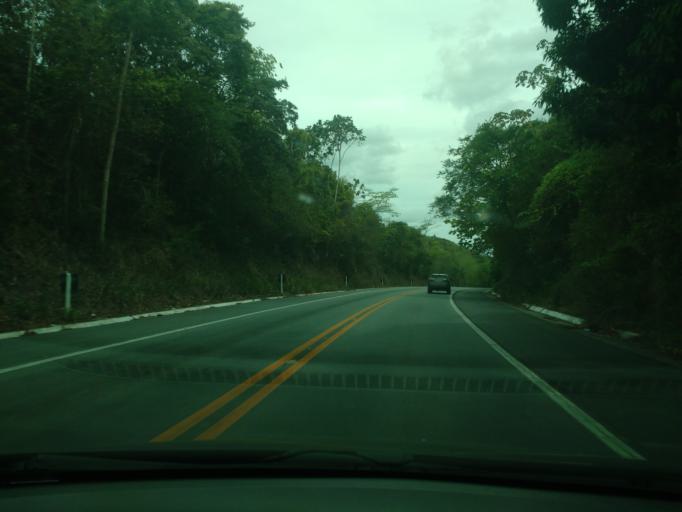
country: BR
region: Alagoas
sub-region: Murici
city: Murici
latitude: -9.2510
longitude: -35.9918
